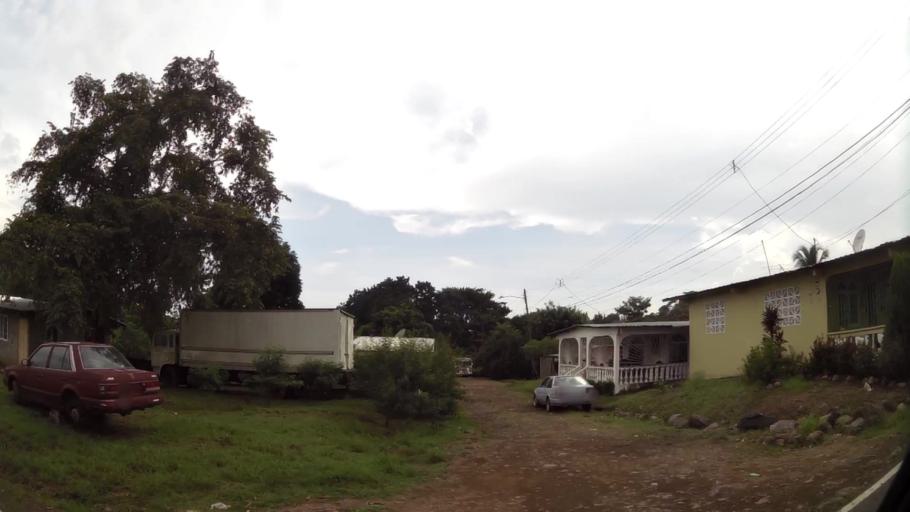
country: PA
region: Panama
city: Tocumen
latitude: 9.1072
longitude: -79.3743
